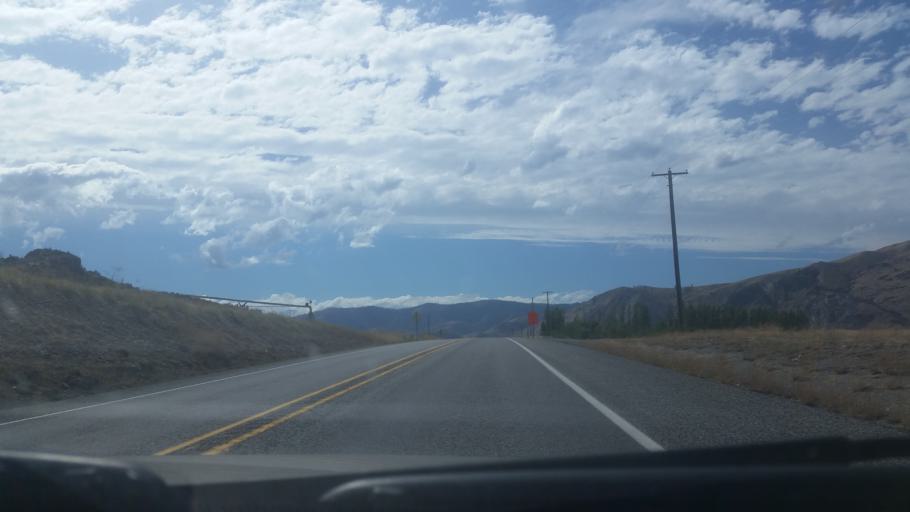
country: US
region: Washington
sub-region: Chelan County
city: Chelan
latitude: 47.7682
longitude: -120.1161
